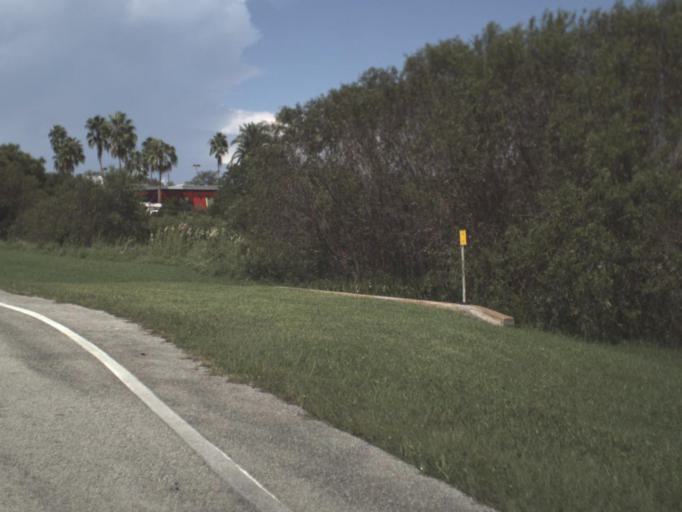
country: US
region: Florida
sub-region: Sarasota County
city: Plantation
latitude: 27.0499
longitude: -82.3897
